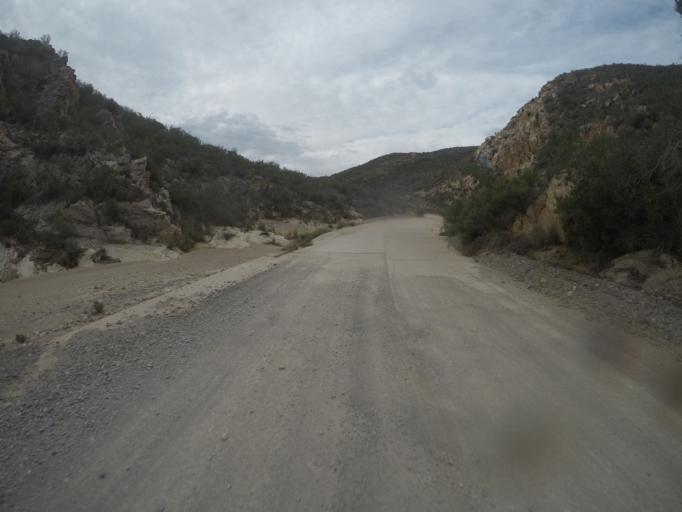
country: ZA
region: Eastern Cape
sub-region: Cacadu District Municipality
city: Willowmore
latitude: -33.5059
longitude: 23.6351
